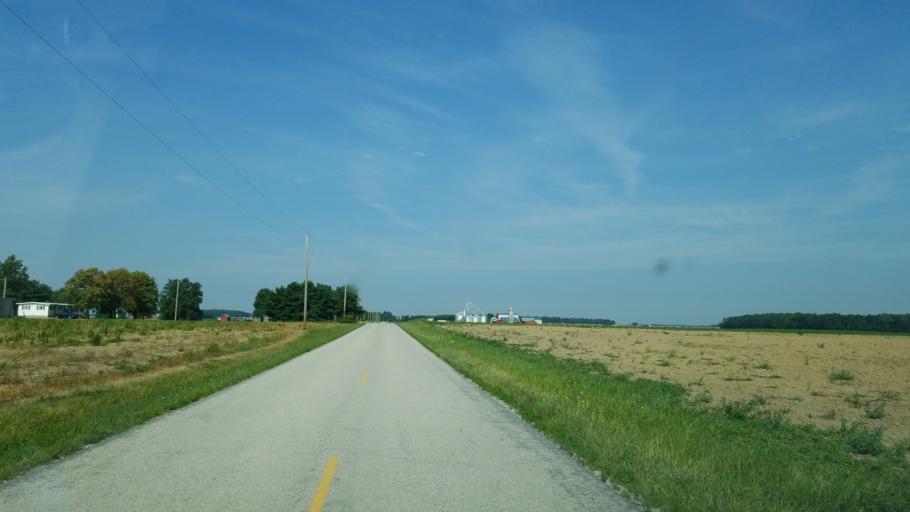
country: US
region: Ohio
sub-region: Huron County
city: Willard
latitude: 41.0227
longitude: -82.8845
